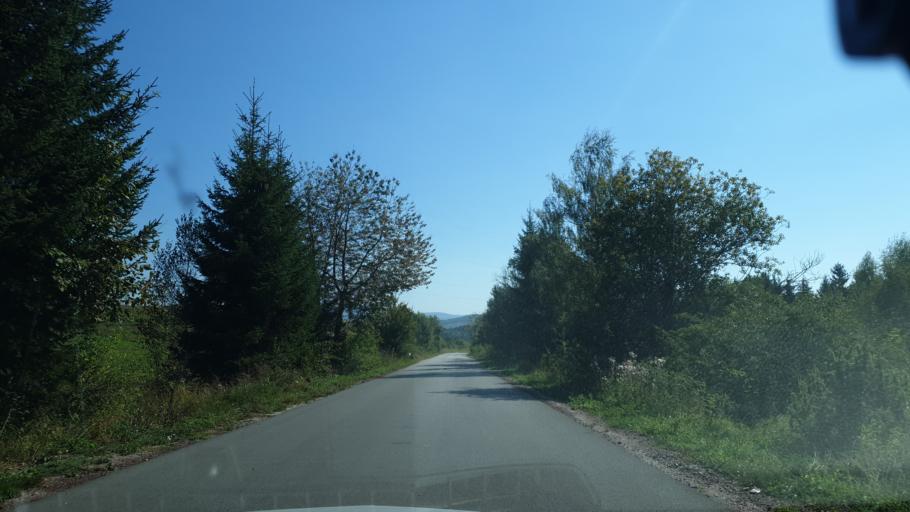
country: RS
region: Central Serbia
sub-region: Zlatiborski Okrug
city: Nova Varos
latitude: 43.4259
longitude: 19.9031
